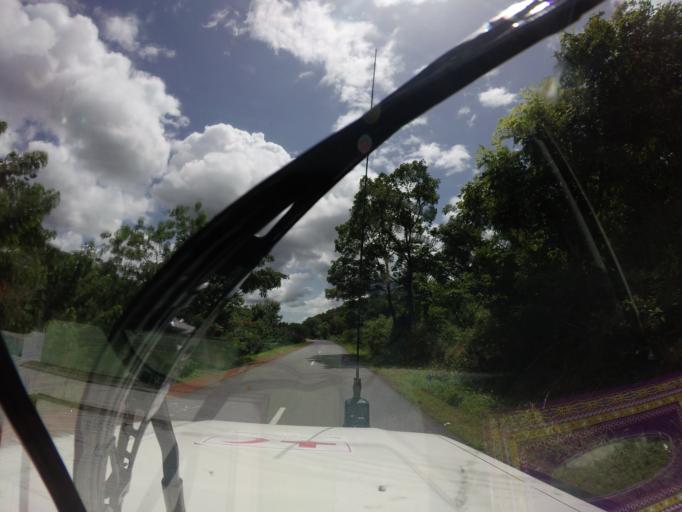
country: SL
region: Northern Province
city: Bindi
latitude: 10.1507
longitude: -11.4706
